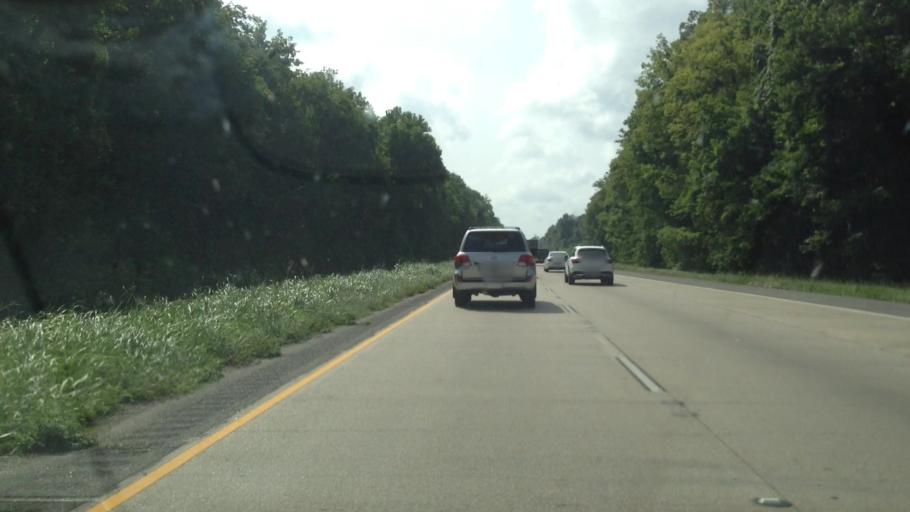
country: US
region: Louisiana
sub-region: Ascension Parish
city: Gonzales
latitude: 30.1891
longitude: -90.9142
